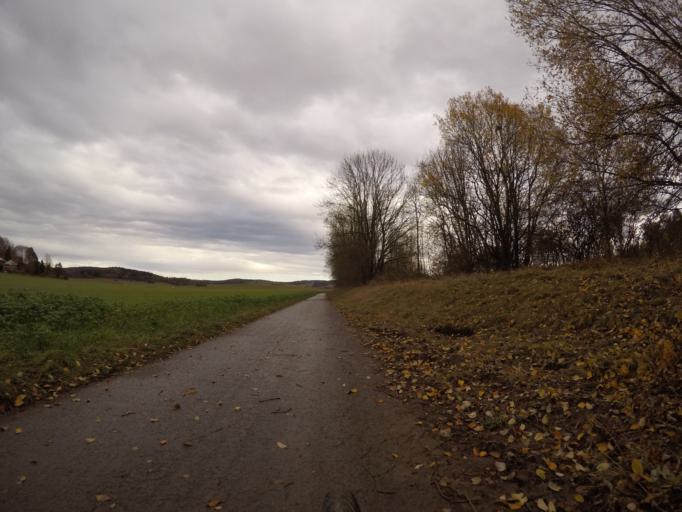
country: DE
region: Baden-Wuerttemberg
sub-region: Tuebingen Region
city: Pfullingen
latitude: 48.4028
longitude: 9.2732
